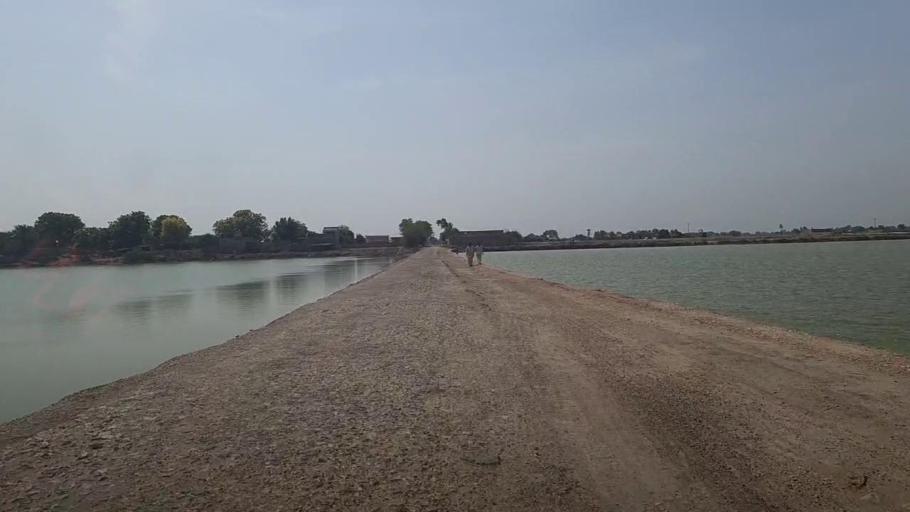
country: PK
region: Sindh
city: Ubauro
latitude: 28.1363
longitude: 69.8269
